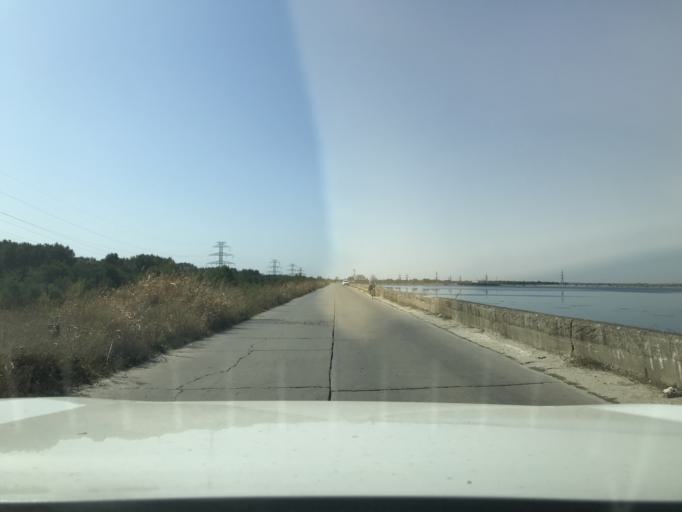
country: RO
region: Olt
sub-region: Municipiul Slatina
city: Slatina
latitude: 44.4027
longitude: 24.3562
